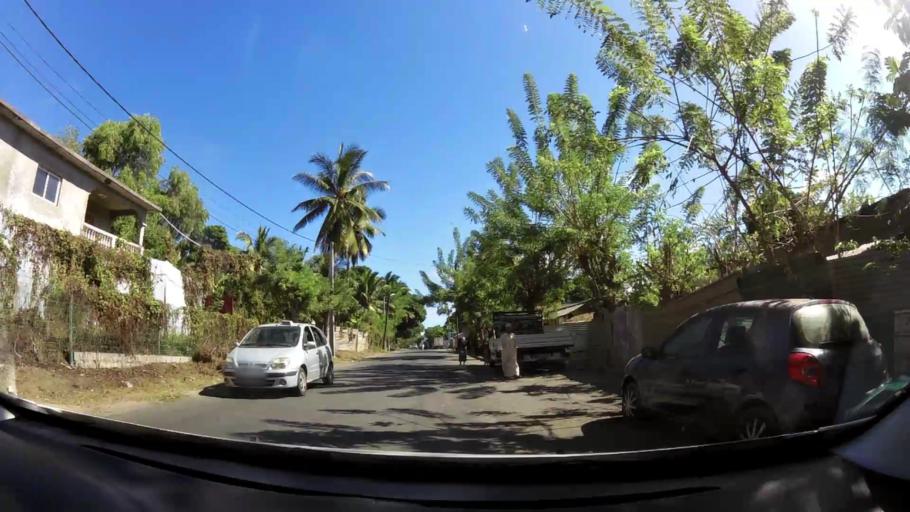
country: YT
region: Pamandzi
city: Pamandzi
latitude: -12.7815
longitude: 45.2783
